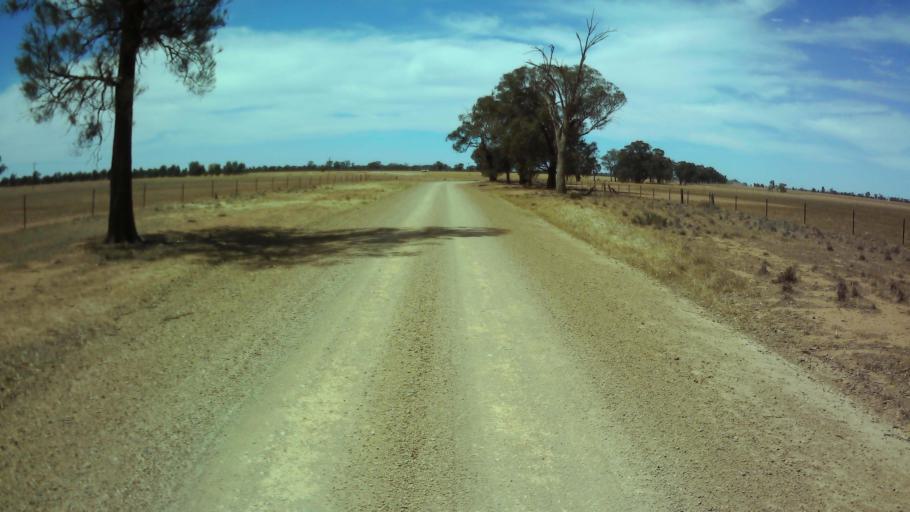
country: AU
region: New South Wales
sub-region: Weddin
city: Grenfell
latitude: -33.8636
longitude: 147.8069
